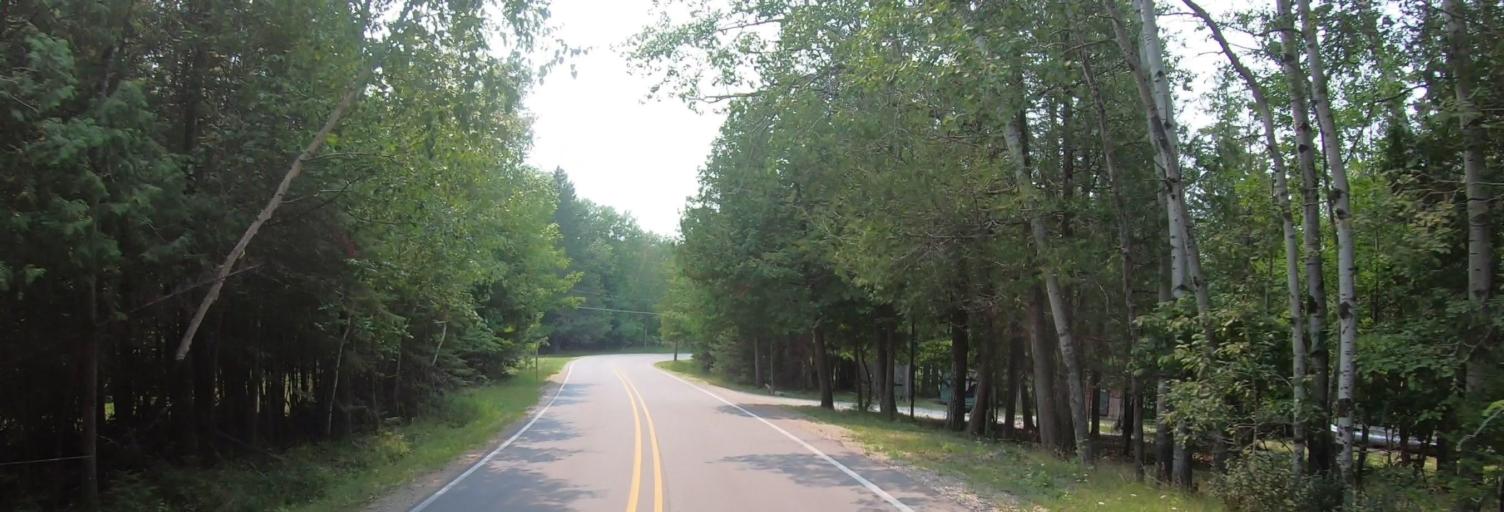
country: CA
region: Ontario
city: Thessalon
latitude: 46.0342
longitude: -83.7255
